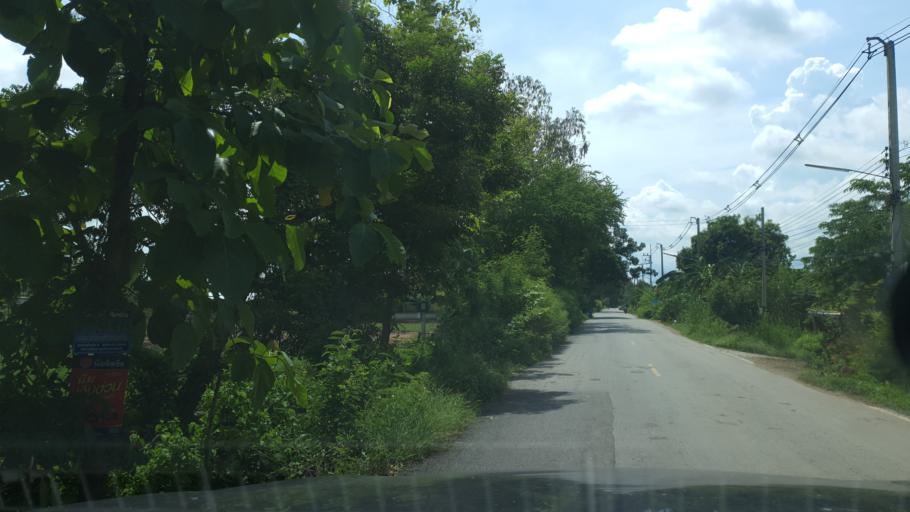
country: TH
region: Sukhothai
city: Sukhothai
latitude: 16.9964
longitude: 99.8441
